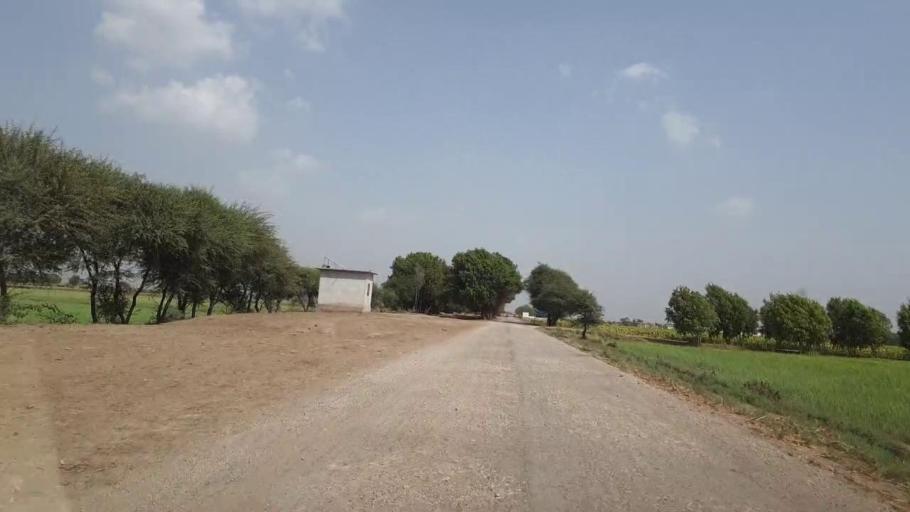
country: PK
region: Sindh
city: Rajo Khanani
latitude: 25.0499
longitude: 68.8719
